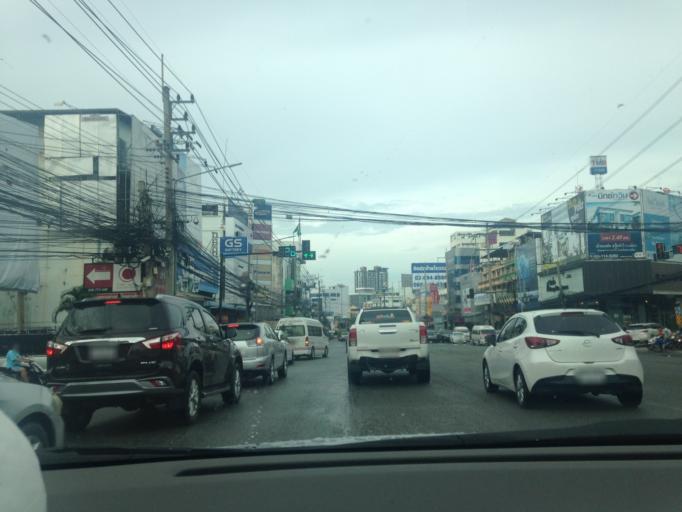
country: TH
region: Chon Buri
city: Si Racha
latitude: 13.1629
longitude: 100.9286
